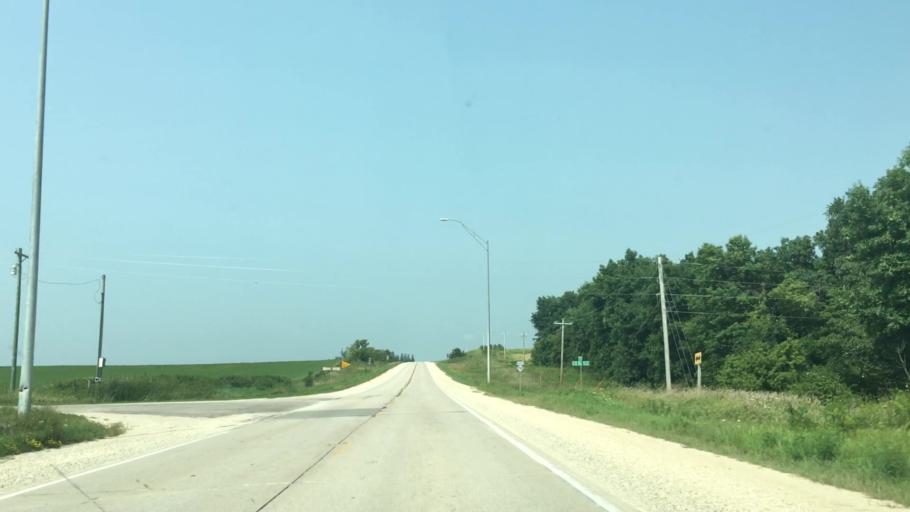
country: US
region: Iowa
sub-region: Fayette County
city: West Union
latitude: 43.1289
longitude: -91.8691
